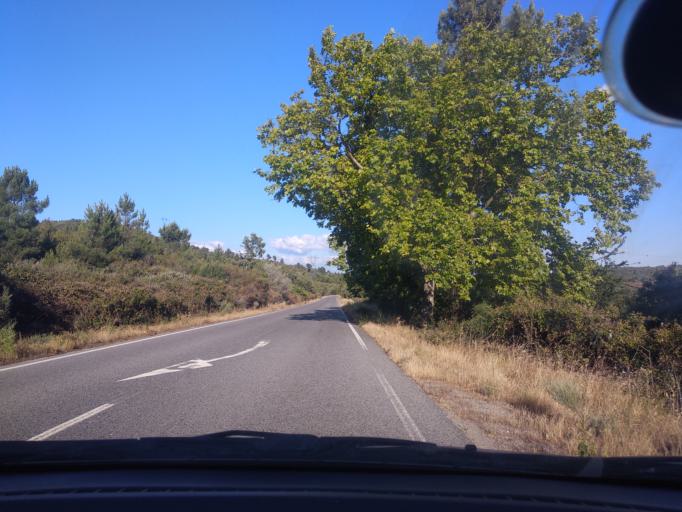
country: PT
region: Castelo Branco
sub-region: Covilha
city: Teixoso
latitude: 40.2344
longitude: -7.3787
